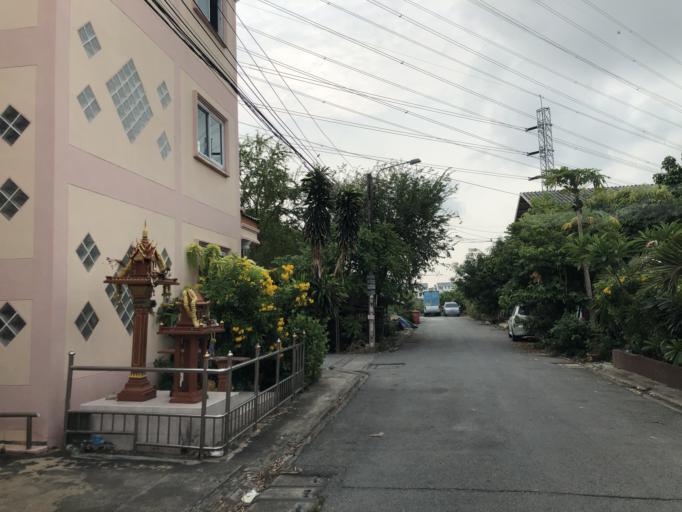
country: TH
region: Bangkok
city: Bang Na
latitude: 13.6040
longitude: 100.6834
